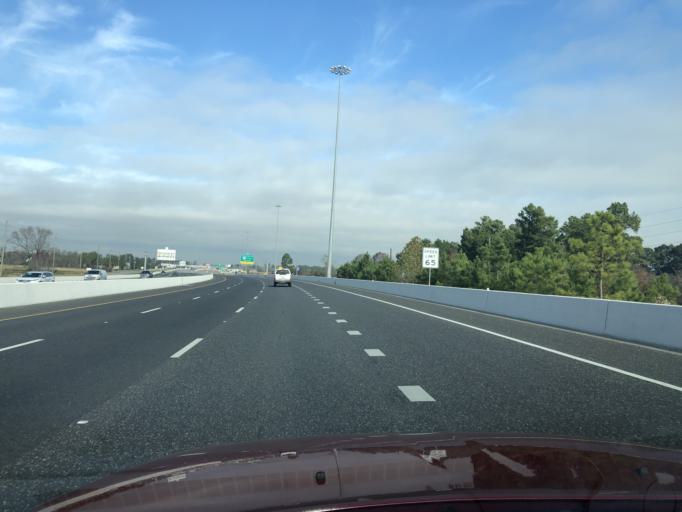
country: US
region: Texas
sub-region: Harris County
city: Tomball
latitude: 30.0585
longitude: -95.6163
